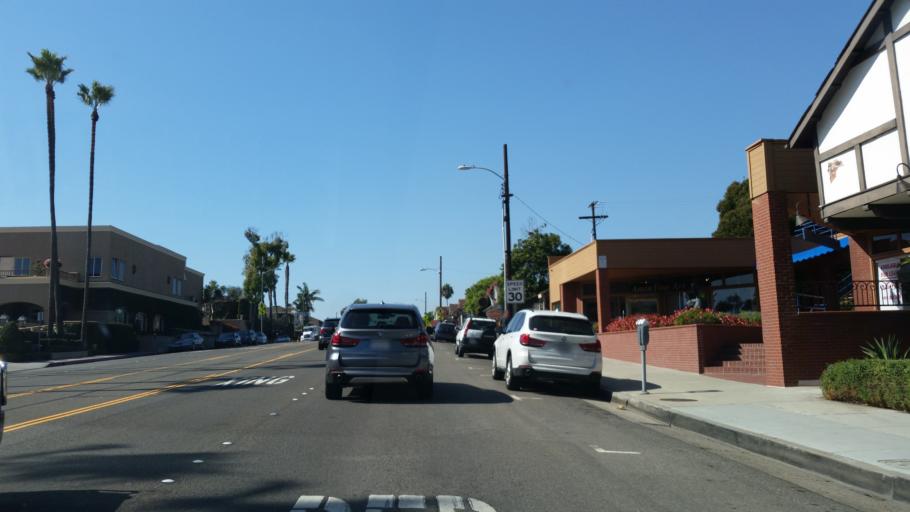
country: US
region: California
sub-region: Orange County
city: Laguna Beach
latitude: 33.5304
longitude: -117.7731
